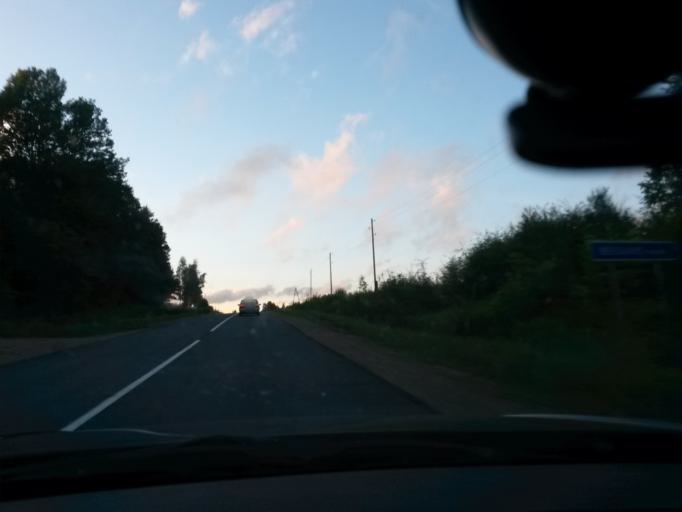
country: LV
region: Madonas Rajons
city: Madona
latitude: 56.7899
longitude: 26.0303
